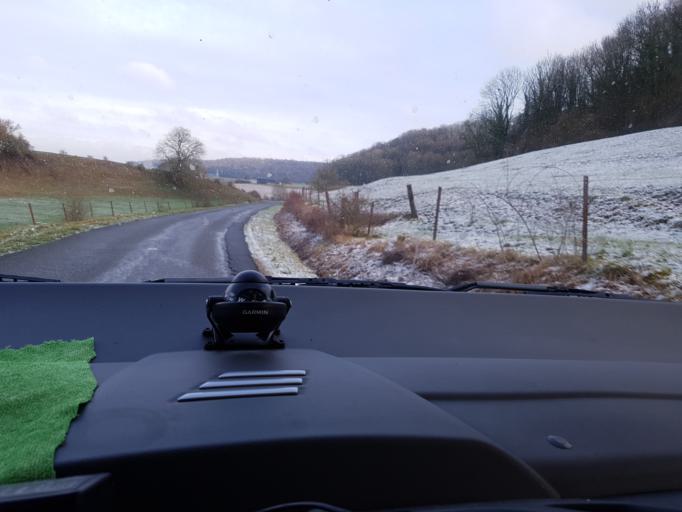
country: FR
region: Champagne-Ardenne
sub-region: Departement des Ardennes
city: Tournes
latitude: 49.7401
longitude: 4.5855
